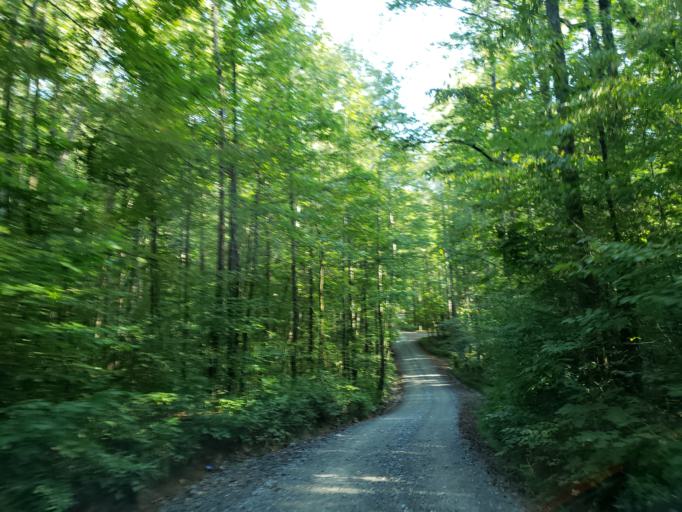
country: US
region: Georgia
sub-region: Fannin County
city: Blue Ridge
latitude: 34.6904
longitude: -84.2698
